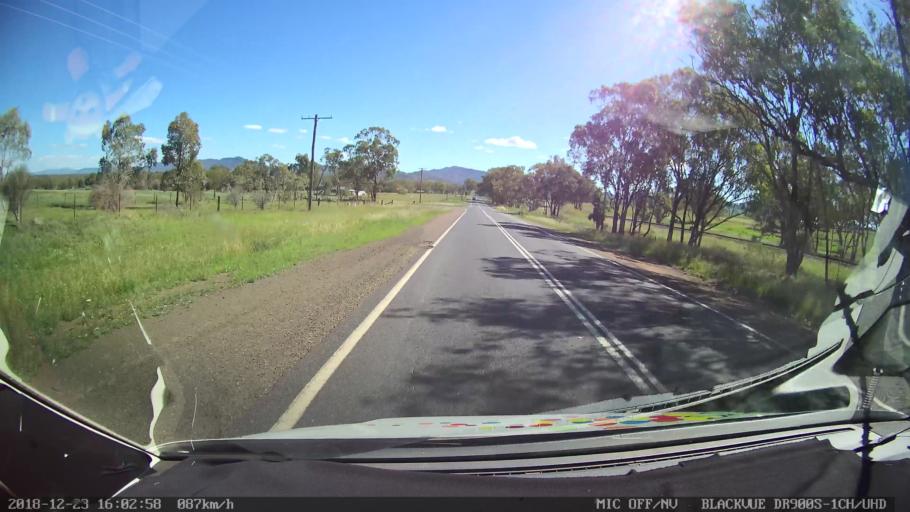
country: AU
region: New South Wales
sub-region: Tamworth Municipality
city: Phillip
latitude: -31.2381
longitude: 150.8047
